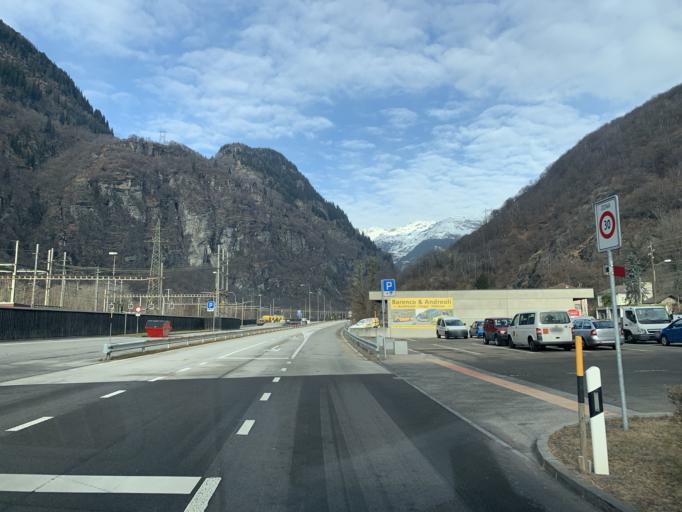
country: CH
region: Ticino
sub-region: Leventina District
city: Faido
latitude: 46.4414
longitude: 8.8396
